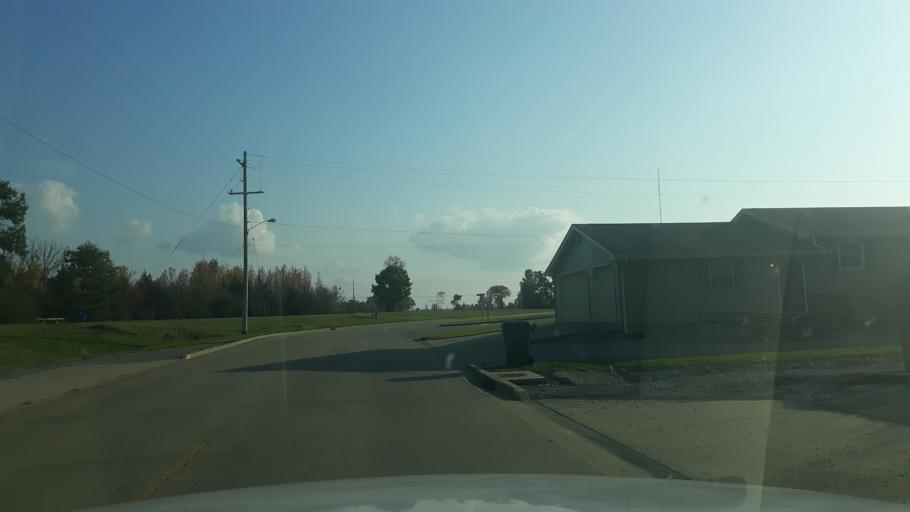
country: US
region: Illinois
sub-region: Saline County
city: Harrisburg
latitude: 37.7231
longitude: -88.5403
